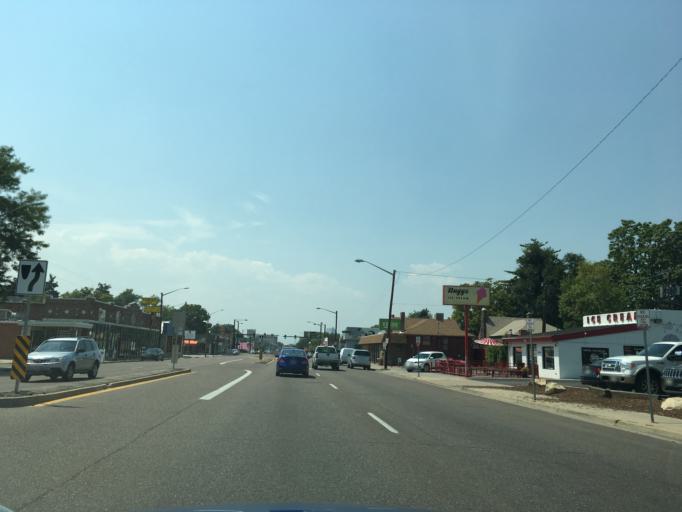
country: US
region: Colorado
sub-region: Arapahoe County
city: Glendale
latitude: 39.7402
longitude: -104.9274
